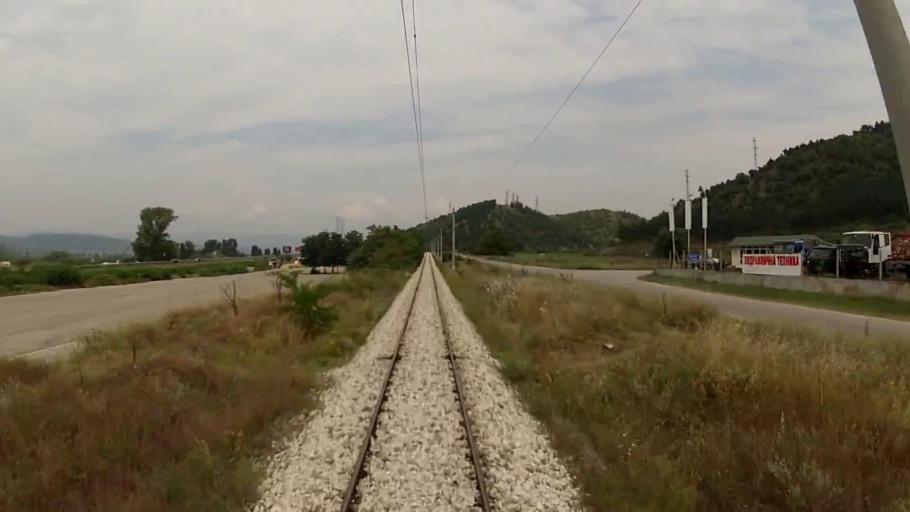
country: BG
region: Blagoevgrad
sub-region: Obshtina Blagoevgrad
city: Blagoevgrad
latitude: 41.9638
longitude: 23.1009
